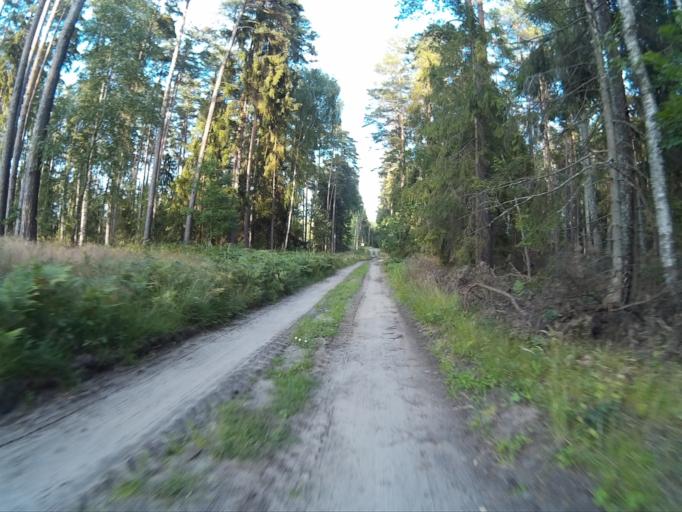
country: PL
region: Kujawsko-Pomorskie
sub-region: Powiat swiecki
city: Lniano
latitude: 53.5634
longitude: 18.1316
